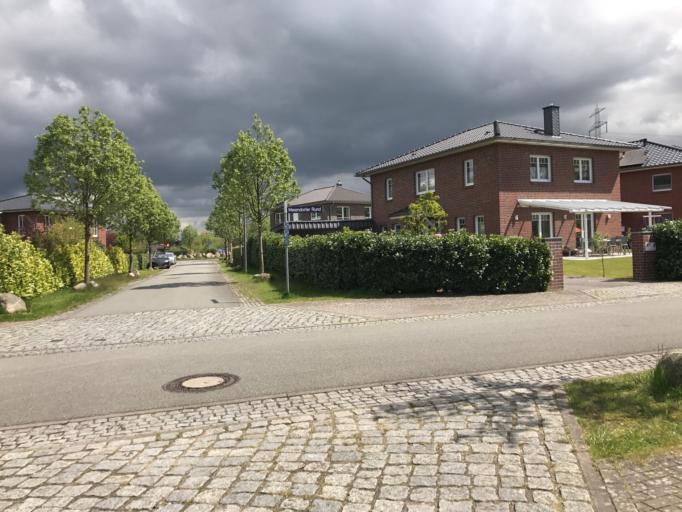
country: DE
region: Schleswig-Holstein
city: Stapelfeld
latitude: 53.6368
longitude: 10.1831
